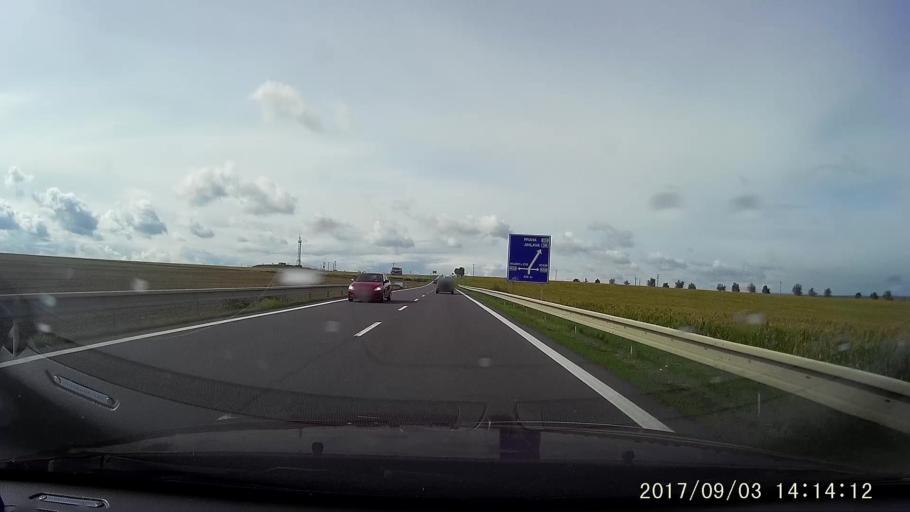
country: CZ
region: South Moravian
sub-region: Okres Znojmo
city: Znojmo
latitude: 48.8832
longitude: 16.0082
